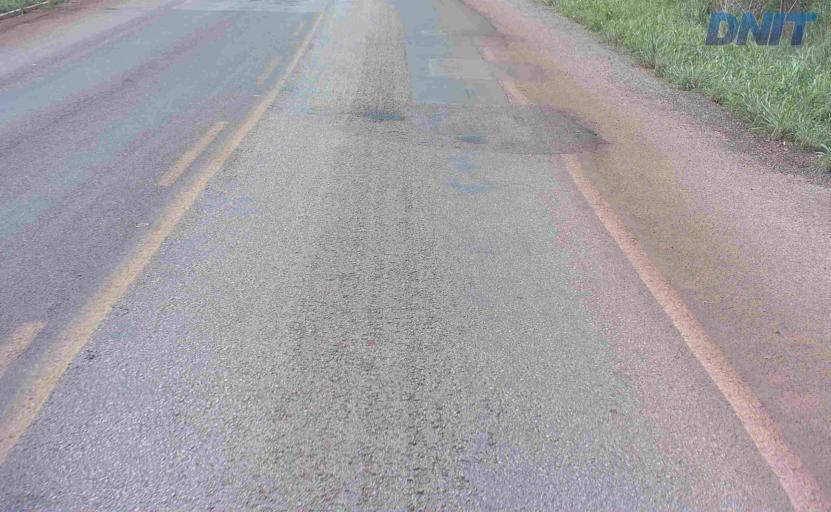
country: BR
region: Goias
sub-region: Barro Alto
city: Barro Alto
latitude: -14.9775
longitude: -48.9297
